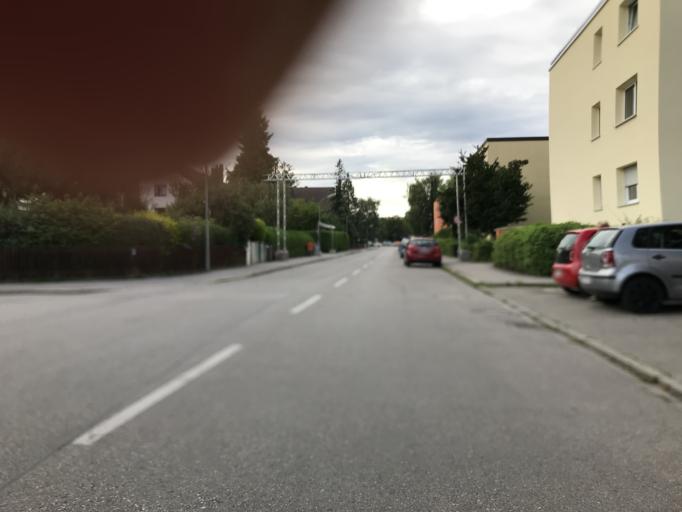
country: DE
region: Bavaria
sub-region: Upper Bavaria
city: Puchheim
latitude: 48.1743
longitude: 11.3517
